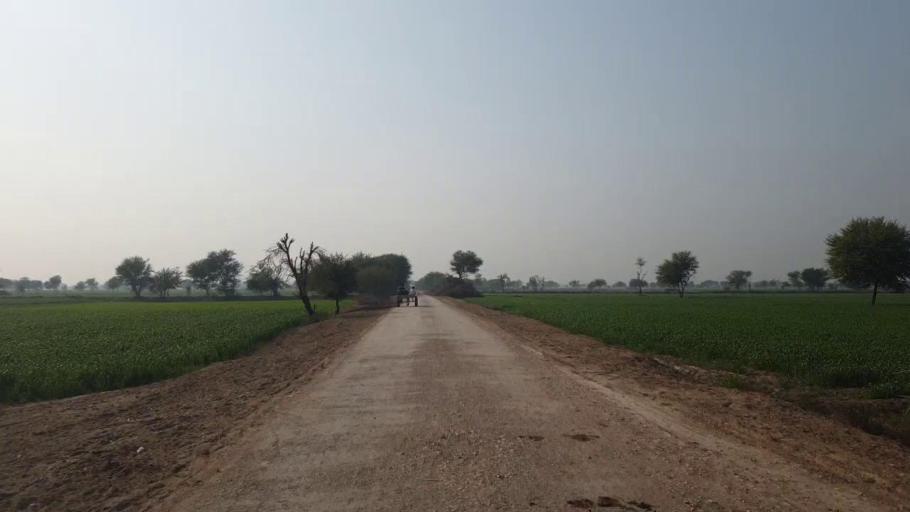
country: PK
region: Sindh
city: Shahdadpur
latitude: 26.0005
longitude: 68.5444
